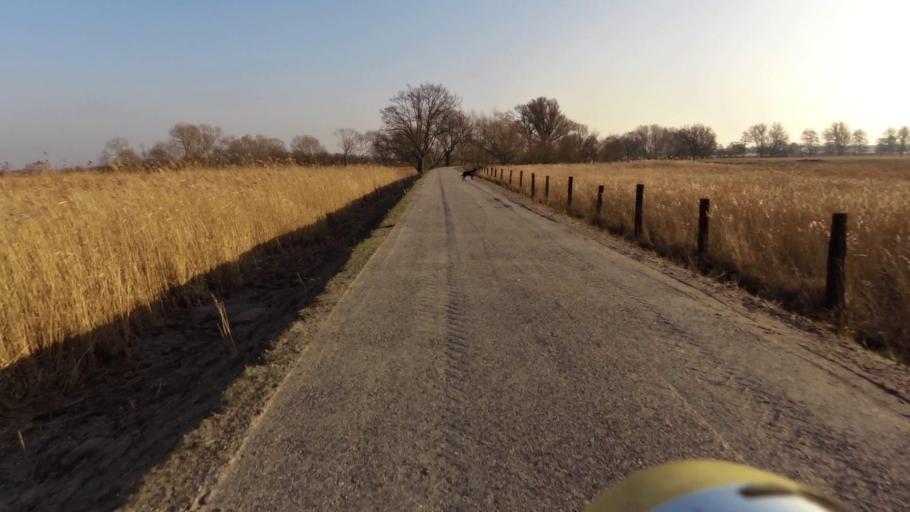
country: PL
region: West Pomeranian Voivodeship
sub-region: Powiat kamienski
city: Wolin
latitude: 53.7542
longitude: 14.5660
